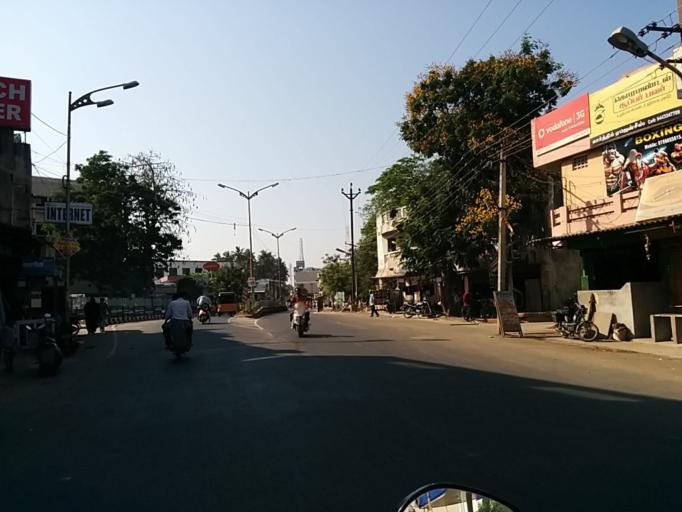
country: IN
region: Pondicherry
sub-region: Puducherry
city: Puducherry
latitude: 11.9521
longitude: 79.8301
